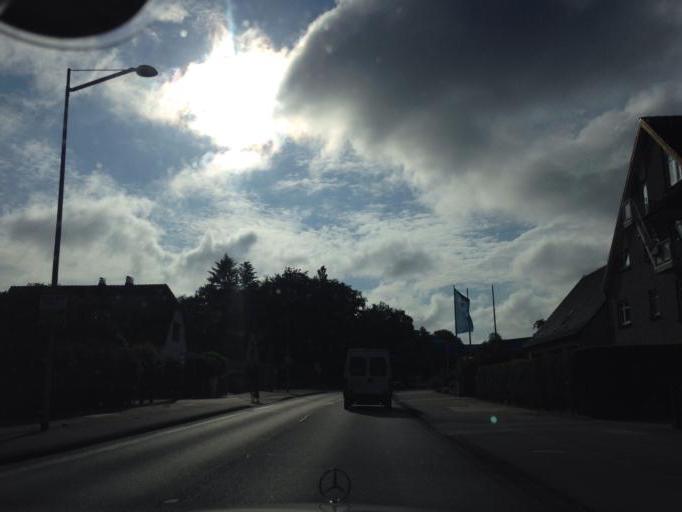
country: DE
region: Schleswig-Holstein
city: Barsbuettel
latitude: 53.5696
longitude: 10.1513
